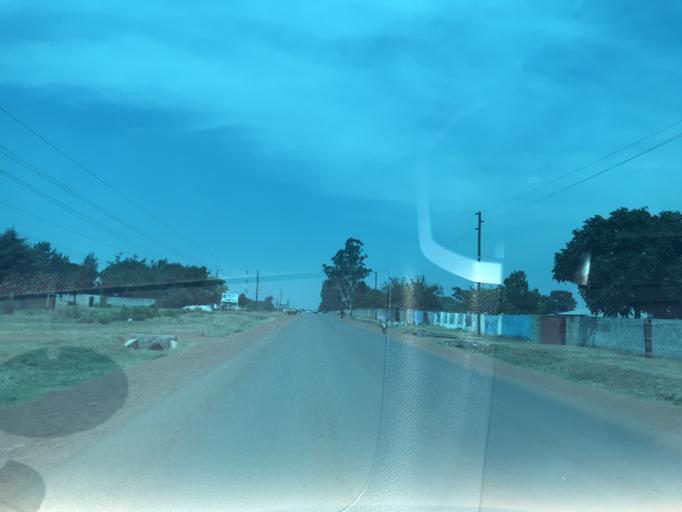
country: ZM
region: Northern
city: Kasama
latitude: -10.2058
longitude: 31.1781
